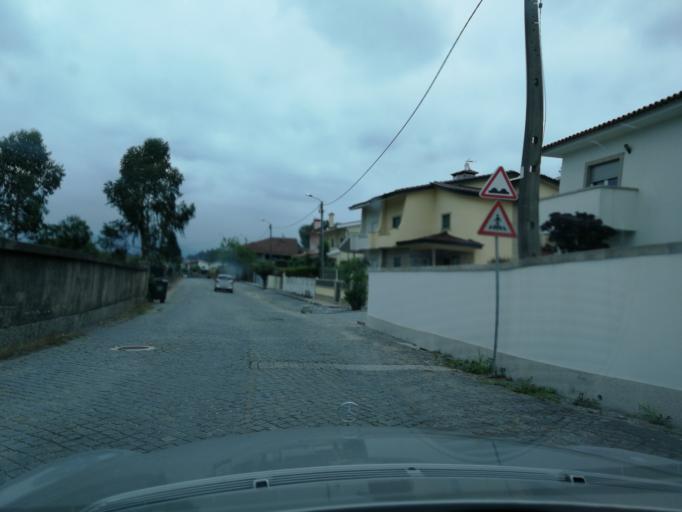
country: PT
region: Braga
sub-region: Vila Verde
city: Prado
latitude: 41.6016
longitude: -8.4371
